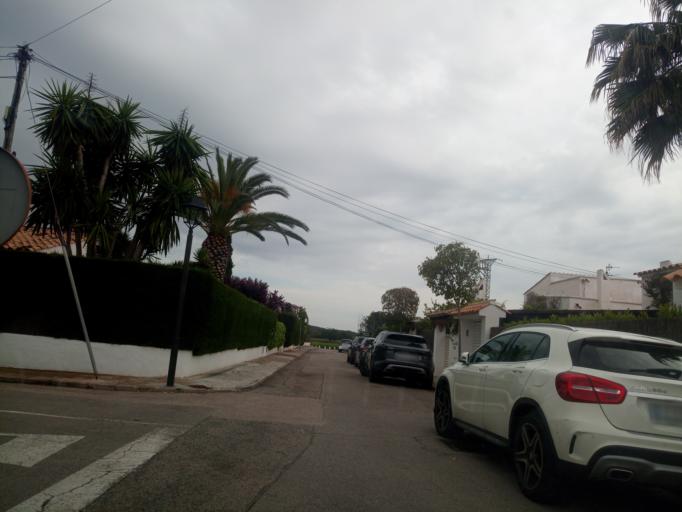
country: ES
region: Catalonia
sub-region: Provincia de Barcelona
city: Sant Pere de Ribes
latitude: 41.2539
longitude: 1.7767
